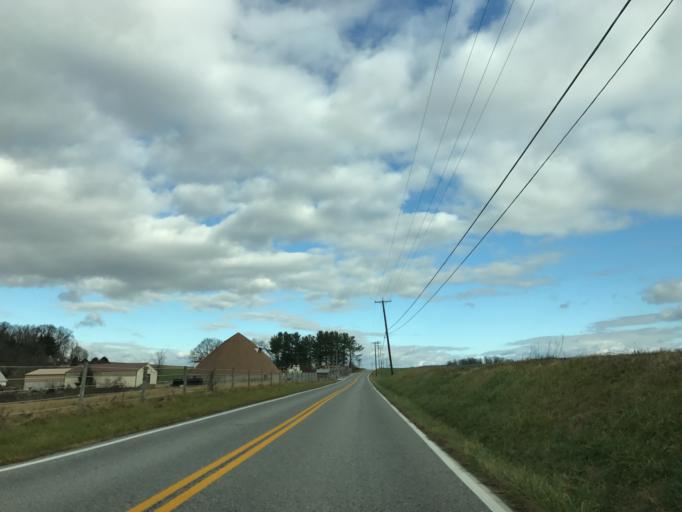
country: US
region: Pennsylvania
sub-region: York County
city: Stewartstown
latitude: 39.6480
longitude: -76.6187
